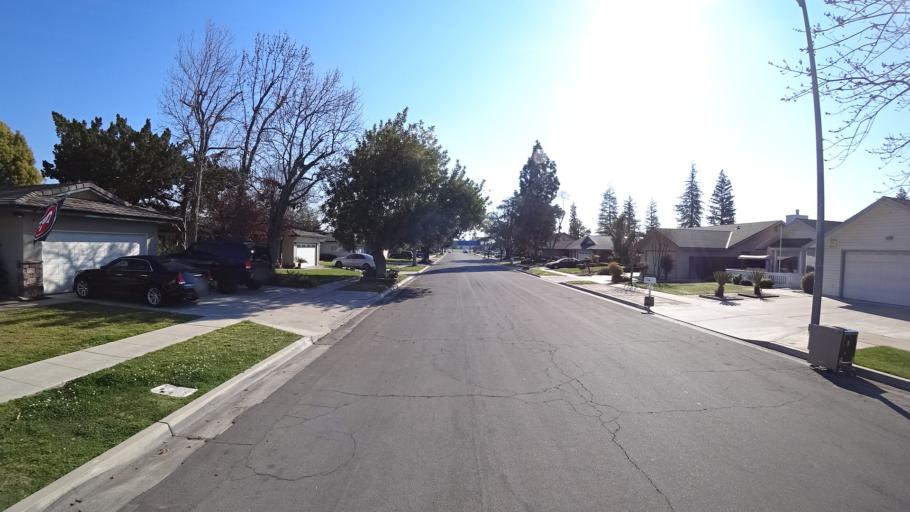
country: US
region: California
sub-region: Fresno County
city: Clovis
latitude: 36.8258
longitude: -119.7750
